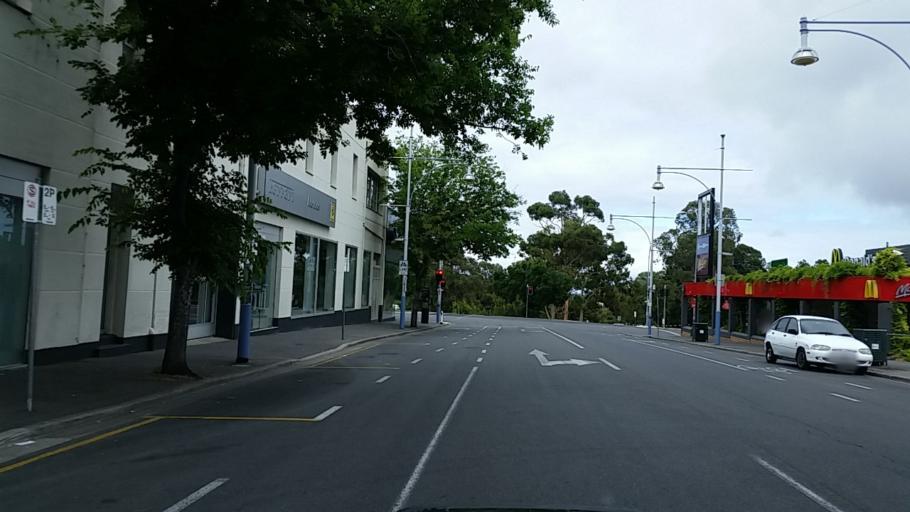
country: AU
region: South Australia
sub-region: Adelaide
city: Adelaide
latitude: -34.9235
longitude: 138.5883
